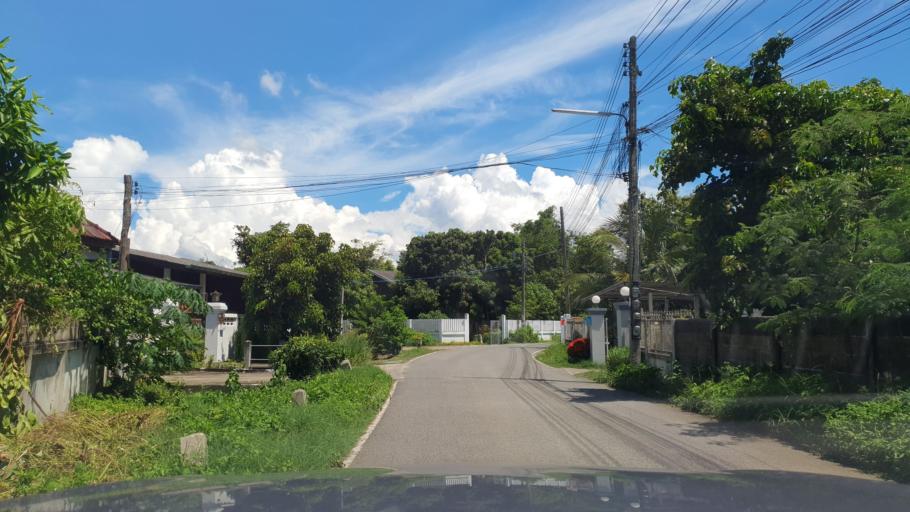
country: TH
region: Chiang Mai
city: San Kamphaeng
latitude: 18.7268
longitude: 99.1325
